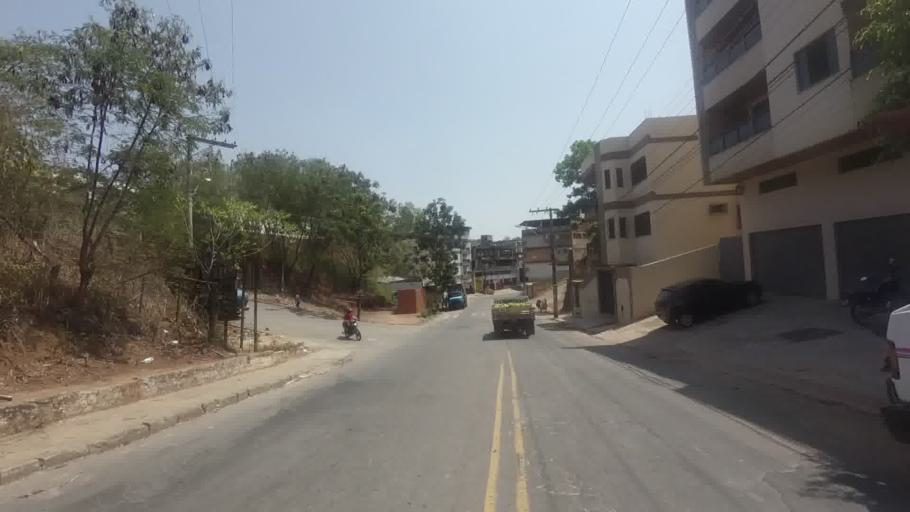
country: BR
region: Espirito Santo
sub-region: Cachoeiro De Itapemirim
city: Cachoeiro de Itapemirim
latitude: -20.8410
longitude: -41.1169
